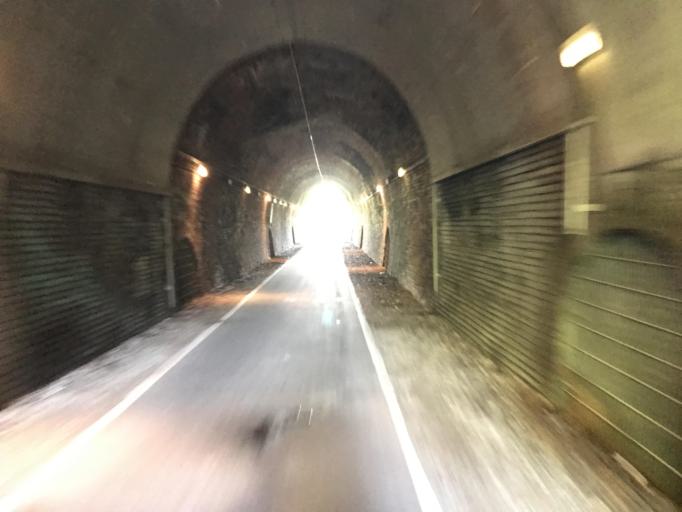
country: DE
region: Hesse
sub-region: Regierungsbezirk Kassel
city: Korbach
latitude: 51.2595
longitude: 8.9159
